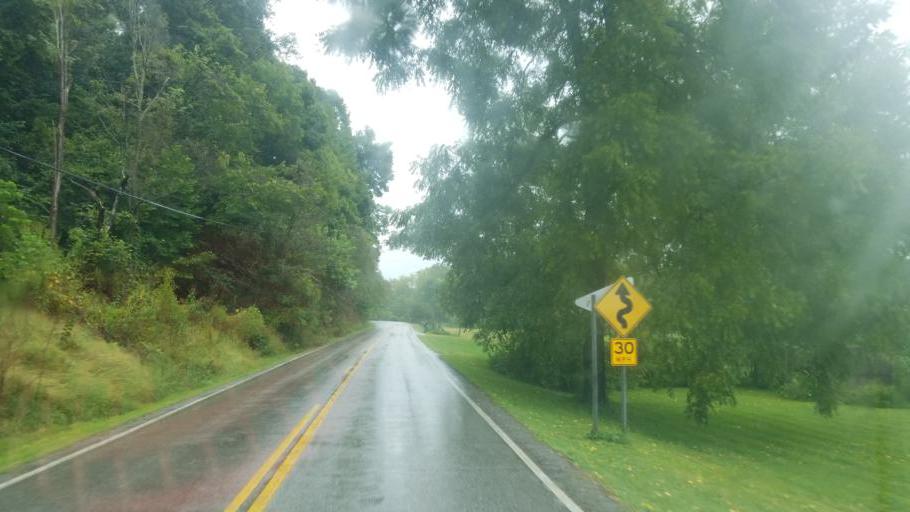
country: US
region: Kentucky
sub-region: Greenup County
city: South Shore
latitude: 38.6575
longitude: -82.9217
